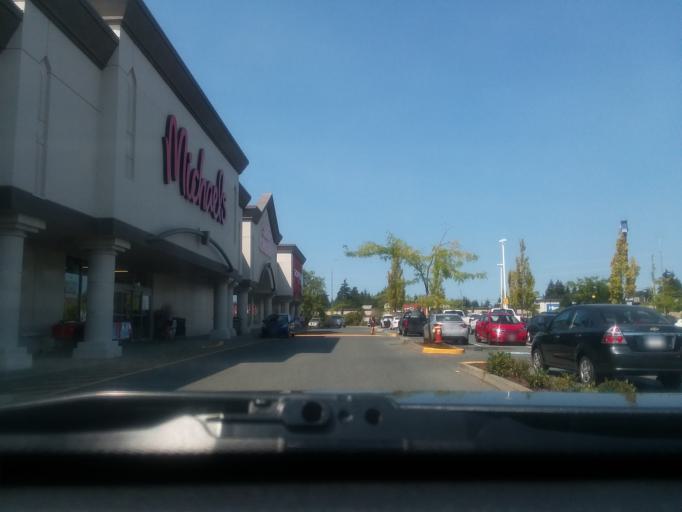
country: CA
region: British Columbia
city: Nanaimo
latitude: 49.2393
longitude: -124.0556
